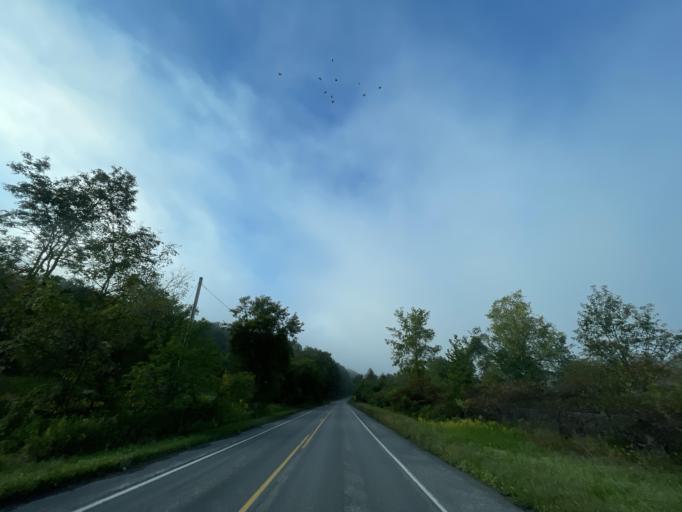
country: US
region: New York
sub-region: Chenango County
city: Oxford
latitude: 42.3865
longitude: -75.6254
